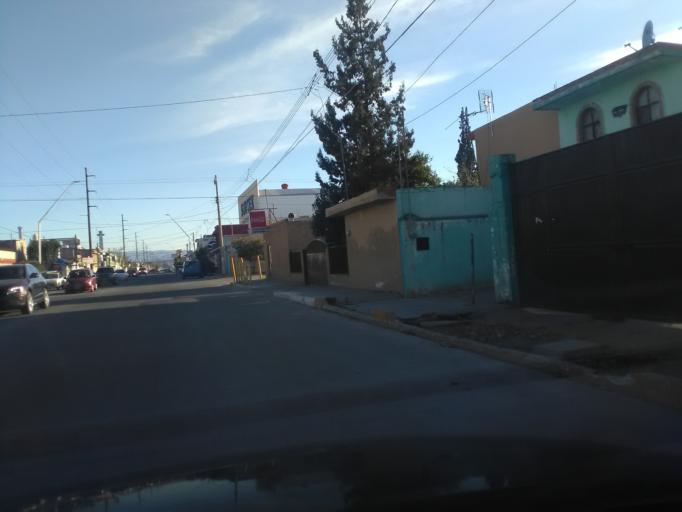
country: MX
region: Durango
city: Victoria de Durango
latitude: 24.0233
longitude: -104.6331
